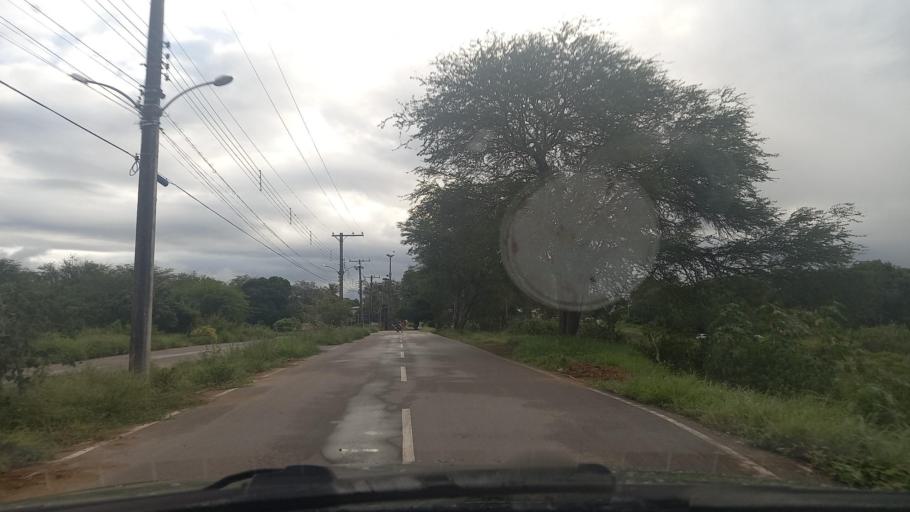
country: BR
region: Bahia
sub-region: Paulo Afonso
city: Paulo Afonso
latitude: -9.3970
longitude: -38.2099
